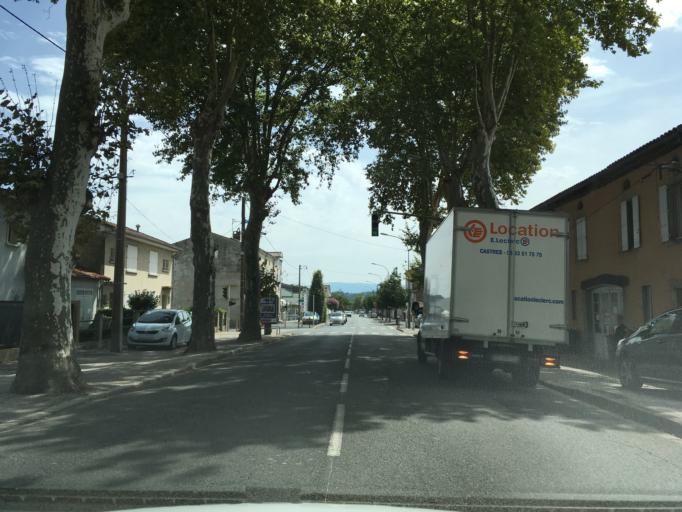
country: FR
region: Midi-Pyrenees
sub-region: Departement du Tarn
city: Castres
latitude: 43.6143
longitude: 2.2322
